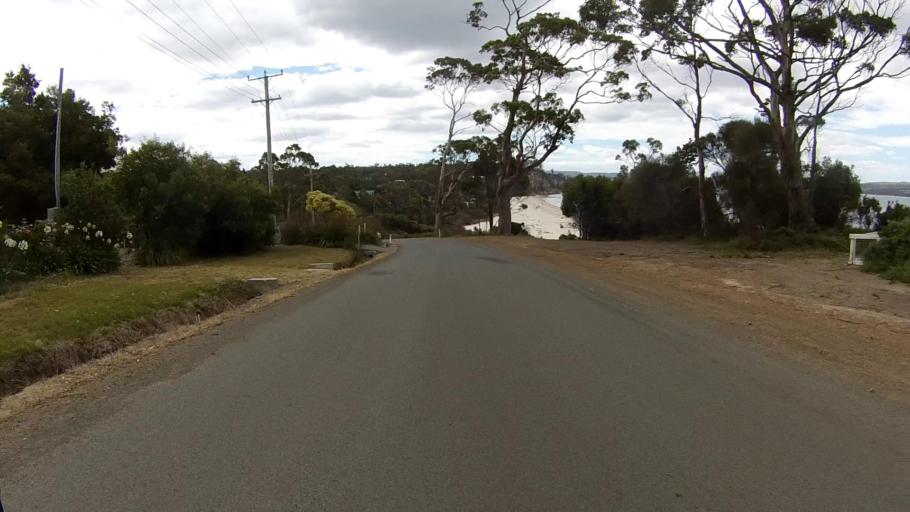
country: AU
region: Tasmania
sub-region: Sorell
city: Sorell
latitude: -42.5831
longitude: 147.9114
